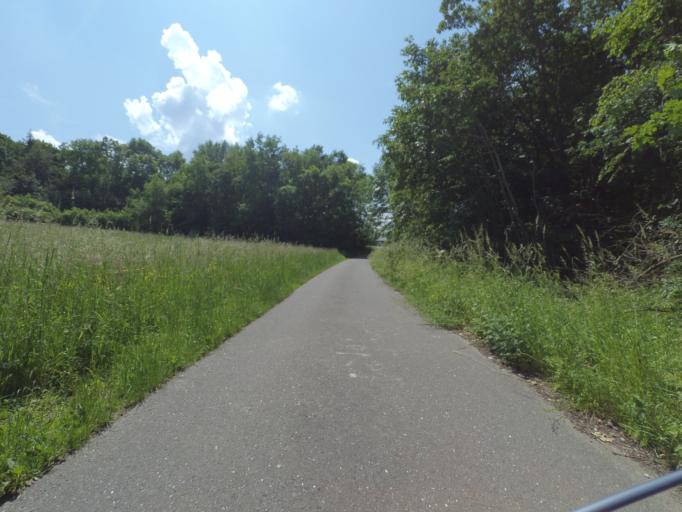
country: DE
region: Rheinland-Pfalz
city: Mermuth
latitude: 50.1631
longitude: 7.4725
